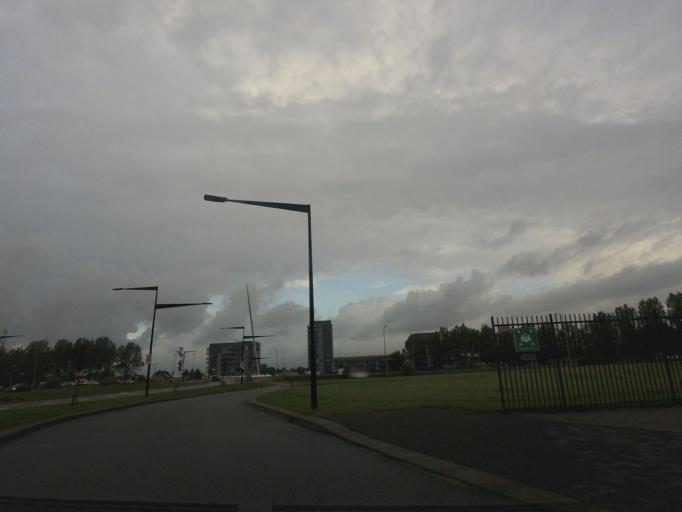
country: NL
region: North Holland
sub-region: Gemeente Haarlemmermeer
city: Hoofddorp
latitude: 52.2898
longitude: 4.6738
